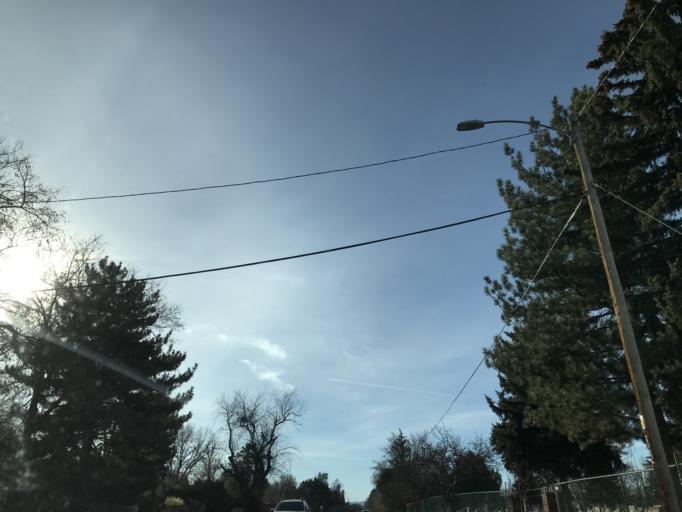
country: US
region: Colorado
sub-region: Arapahoe County
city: Littleton
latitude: 39.6035
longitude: -105.0163
